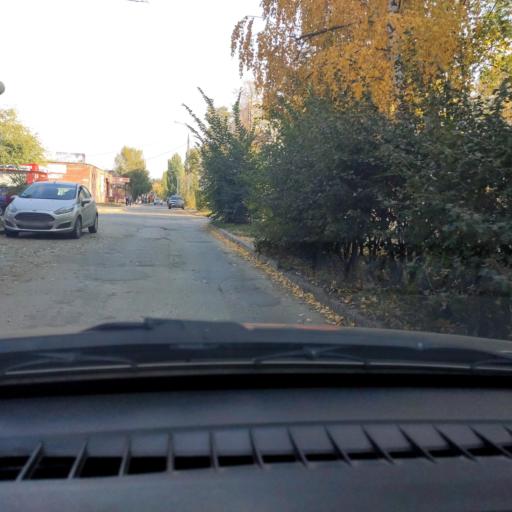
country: RU
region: Samara
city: Tol'yatti
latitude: 53.5104
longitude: 49.2611
